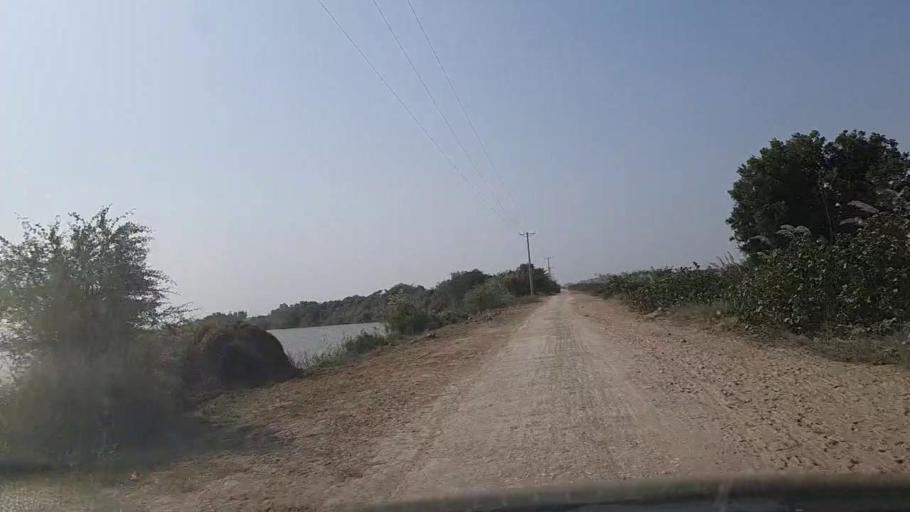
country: PK
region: Sindh
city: Gharo
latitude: 24.6886
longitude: 67.6073
